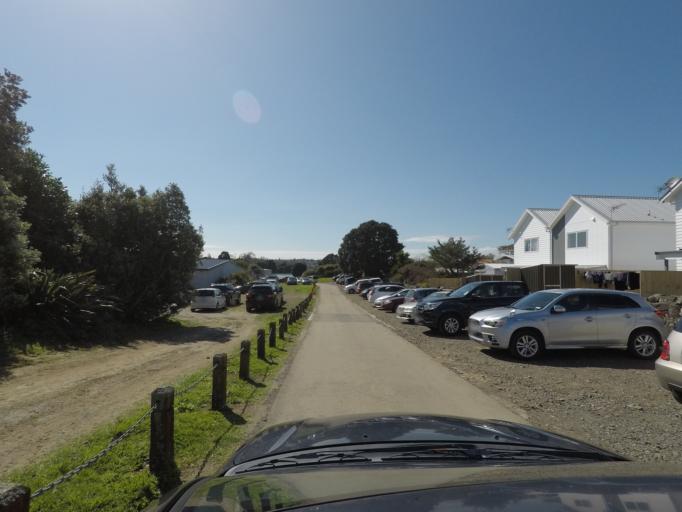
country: NZ
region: Auckland
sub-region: Auckland
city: Tamaki
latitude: -36.9237
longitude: 174.8589
